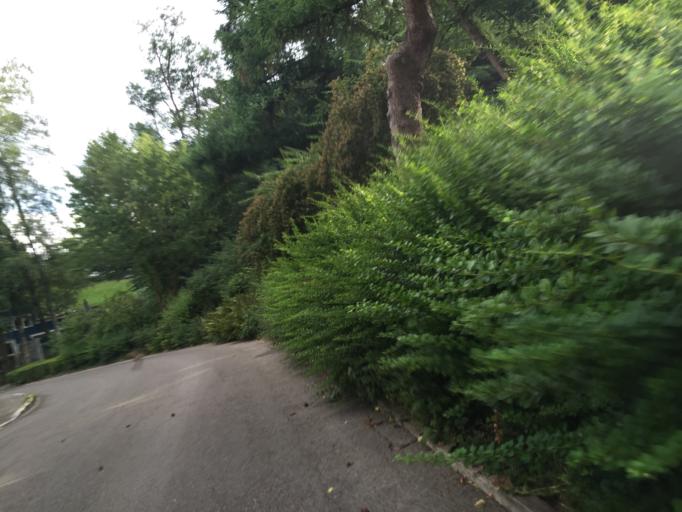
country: CH
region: Bern
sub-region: Bern-Mittelland District
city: Koniz
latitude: 46.9340
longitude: 7.4304
